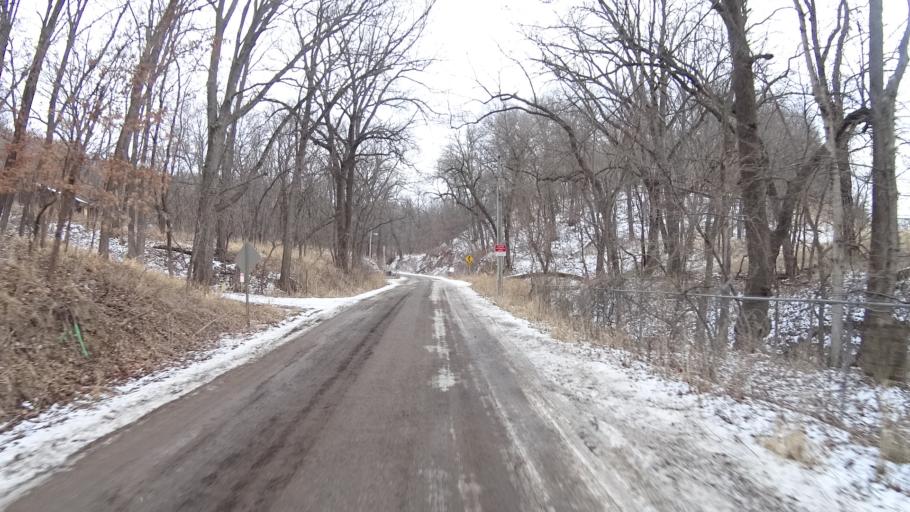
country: US
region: Nebraska
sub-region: Sarpy County
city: Bellevue
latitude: 41.1716
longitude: -95.9066
